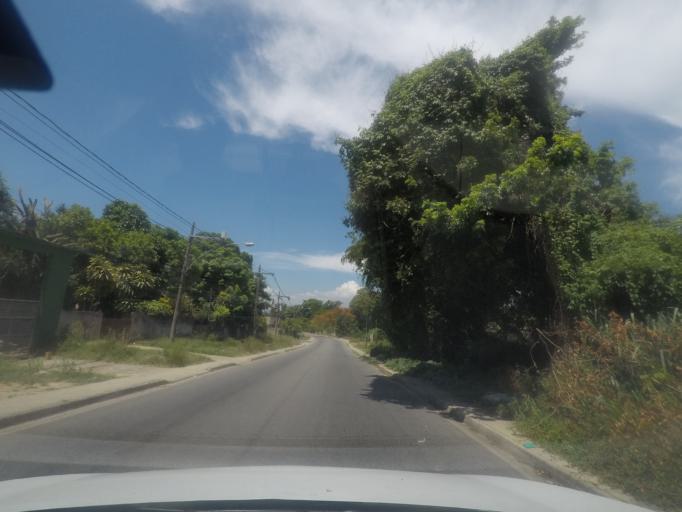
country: BR
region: Rio de Janeiro
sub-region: Itaguai
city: Itaguai
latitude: -22.9807
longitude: -43.6833
